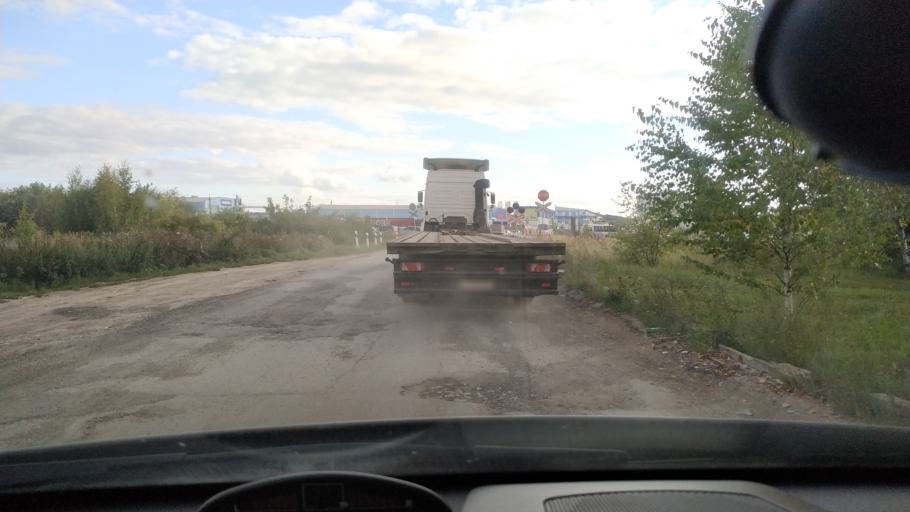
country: RU
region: Rjazan
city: Polyany
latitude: 54.5802
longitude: 39.8388
